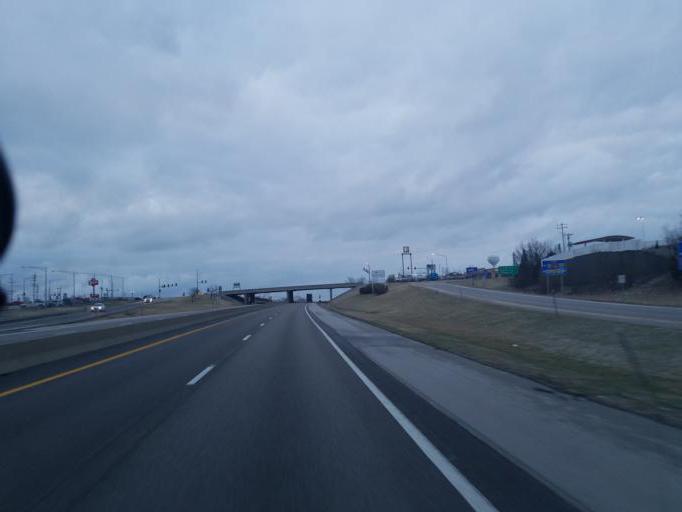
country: US
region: Missouri
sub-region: Warren County
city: Warrenton
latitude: 38.8215
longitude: -91.1418
